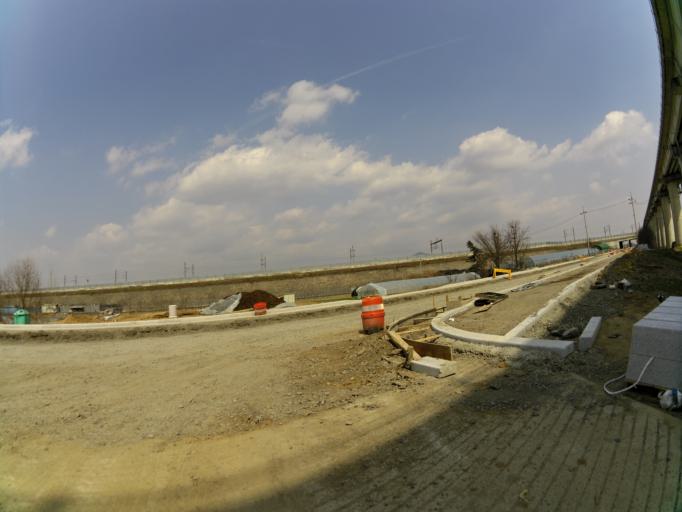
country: KR
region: Gyeongsangbuk-do
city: Gyeongsan-si
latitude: 35.8528
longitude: 128.7141
